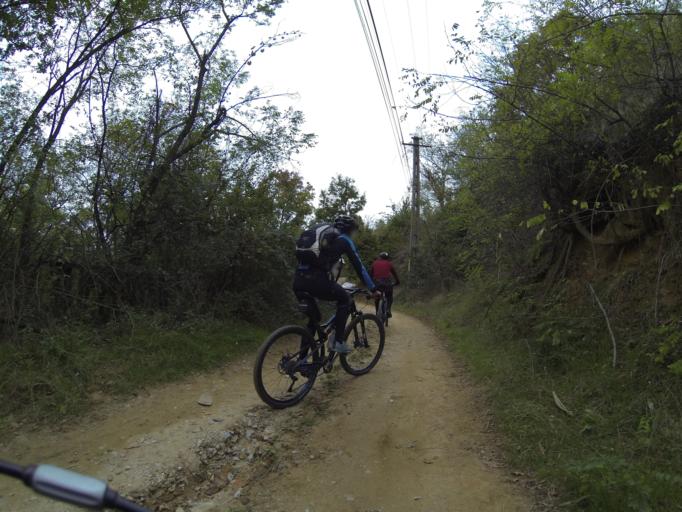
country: RO
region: Gorj
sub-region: Comuna Tismana
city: Sohodol
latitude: 45.0589
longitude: 22.8787
